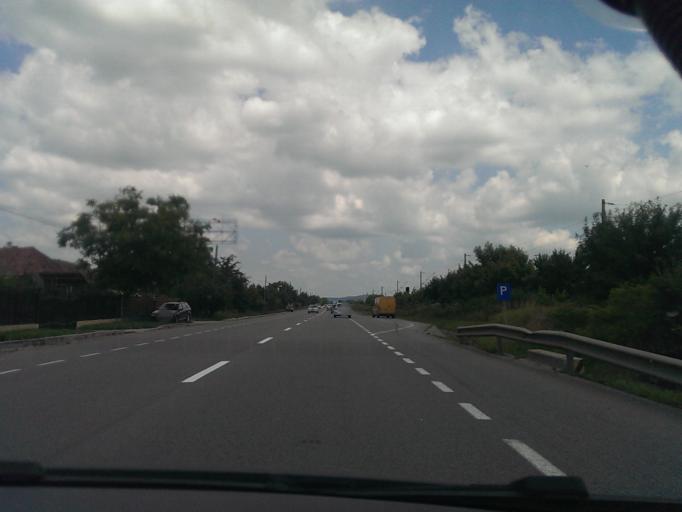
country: RO
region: Cluj
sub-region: Comuna Apahida
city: Apahida
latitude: 46.8436
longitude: 23.7508
